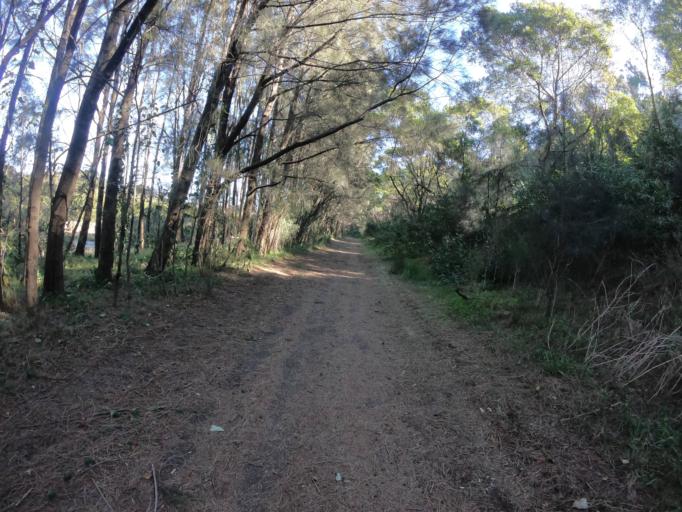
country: AU
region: New South Wales
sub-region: Wollongong
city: Coniston
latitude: -34.4424
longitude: 150.8934
